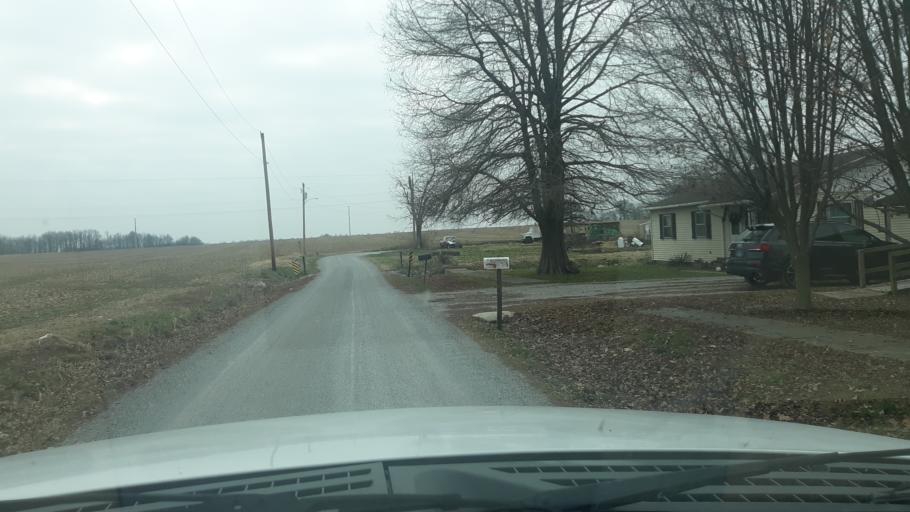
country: US
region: Illinois
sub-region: Saline County
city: Harrisburg
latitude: 37.8352
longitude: -88.6121
